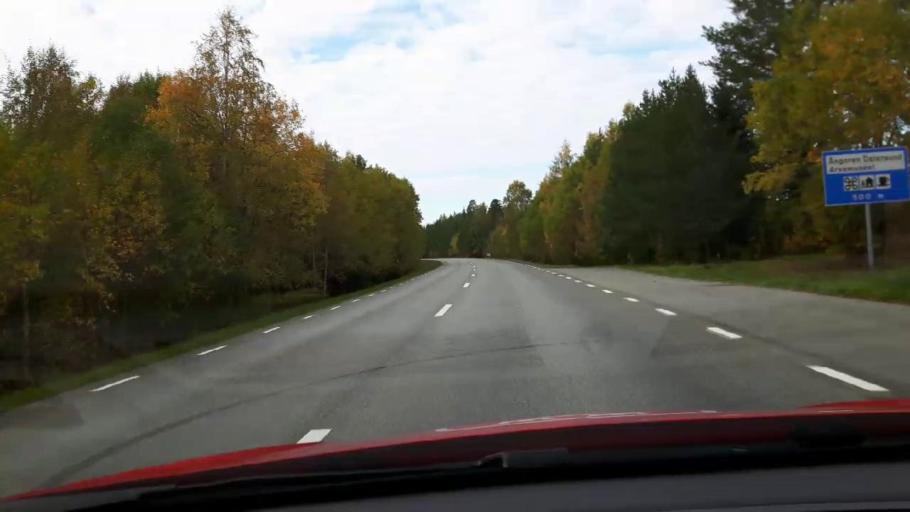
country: SE
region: Jaemtland
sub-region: Krokoms Kommun
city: Valla
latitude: 63.2549
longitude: 13.9944
